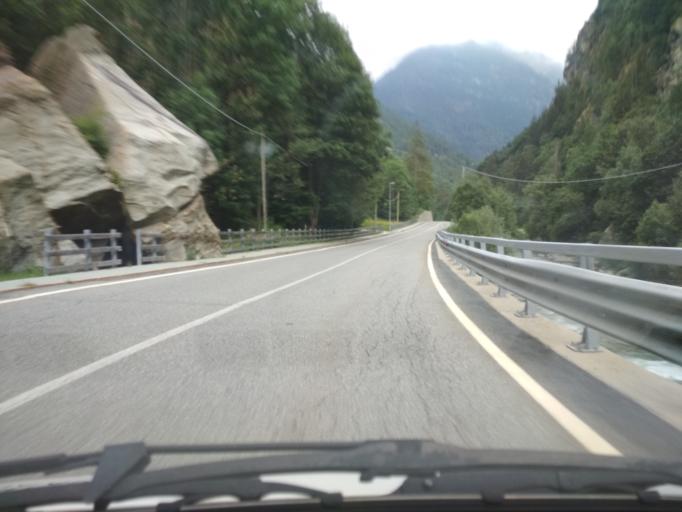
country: IT
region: Aosta Valley
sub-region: Valle d'Aosta
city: Gaby
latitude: 45.7260
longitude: 7.8670
